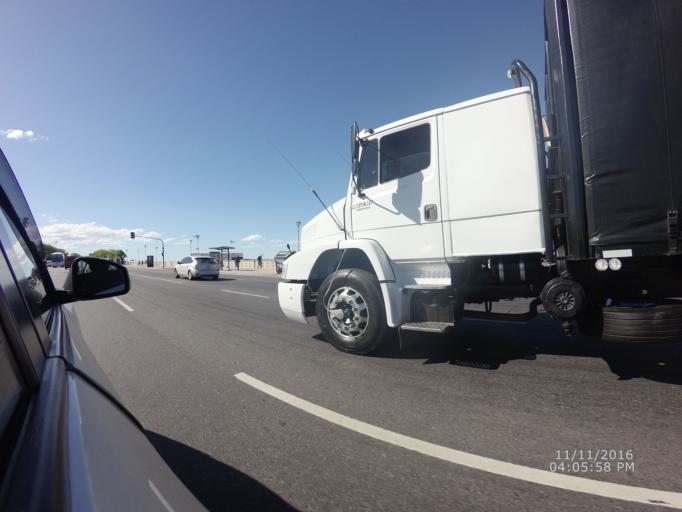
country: AR
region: Buenos Aires F.D.
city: Retiro
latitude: -34.5636
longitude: -58.4043
